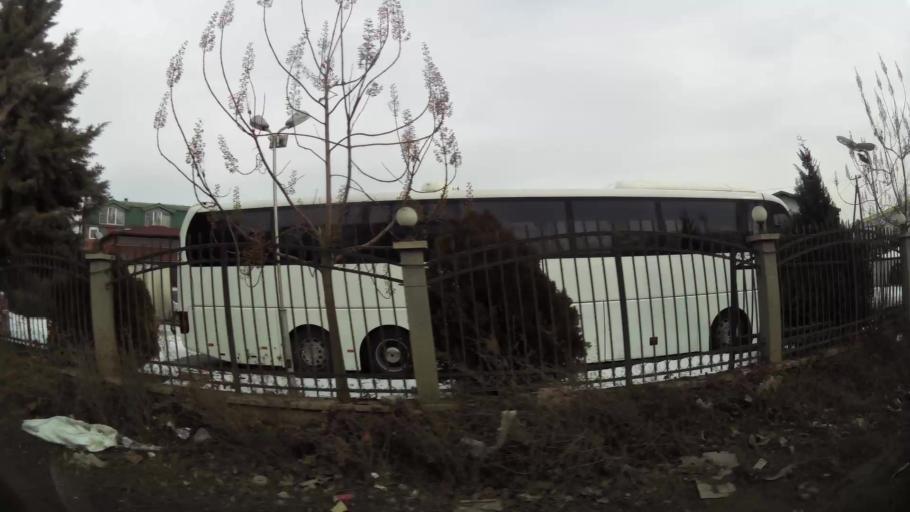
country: MK
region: Suto Orizari
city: Suto Orizare
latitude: 42.0347
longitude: 21.4005
